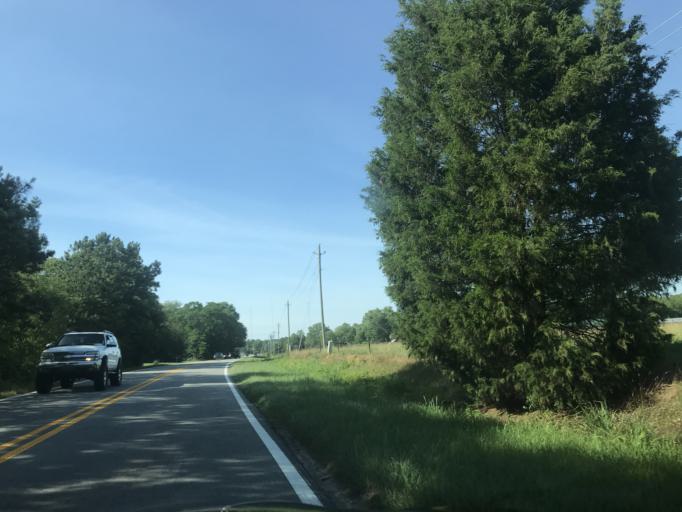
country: US
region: North Carolina
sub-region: Johnston County
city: Clayton
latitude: 35.6122
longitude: -78.5356
